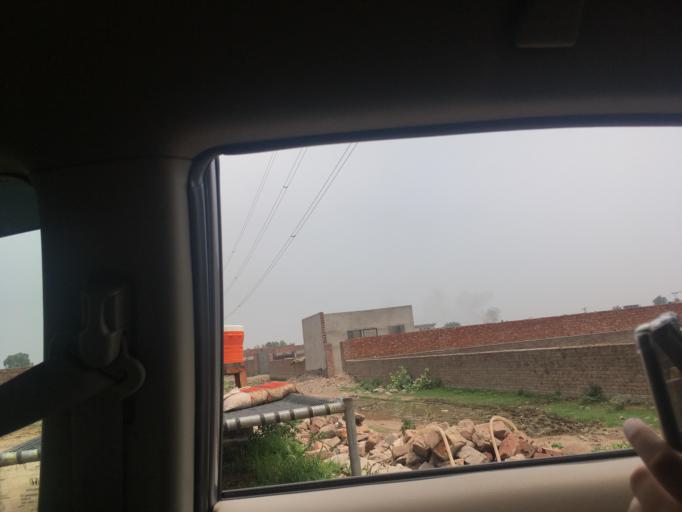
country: PK
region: Punjab
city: Lahore
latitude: 31.6255
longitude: 74.3479
